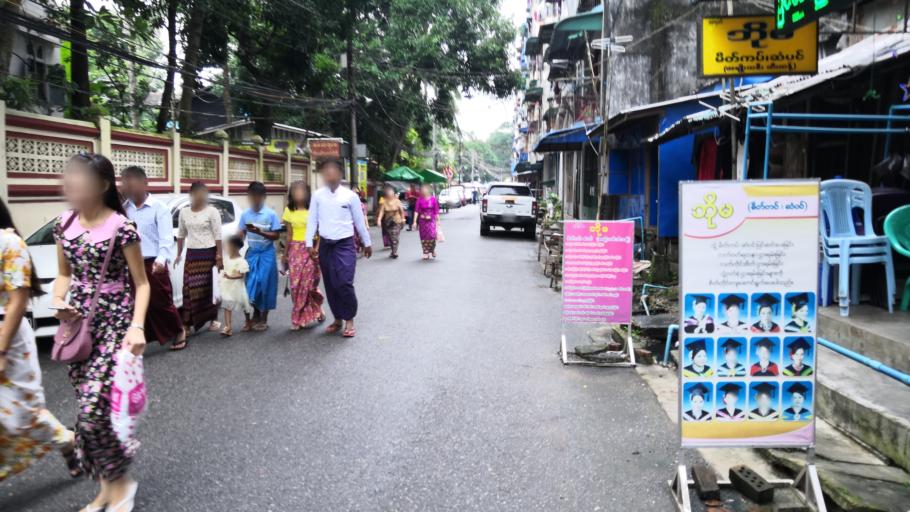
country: MM
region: Yangon
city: Yangon
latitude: 16.7981
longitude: 96.1552
